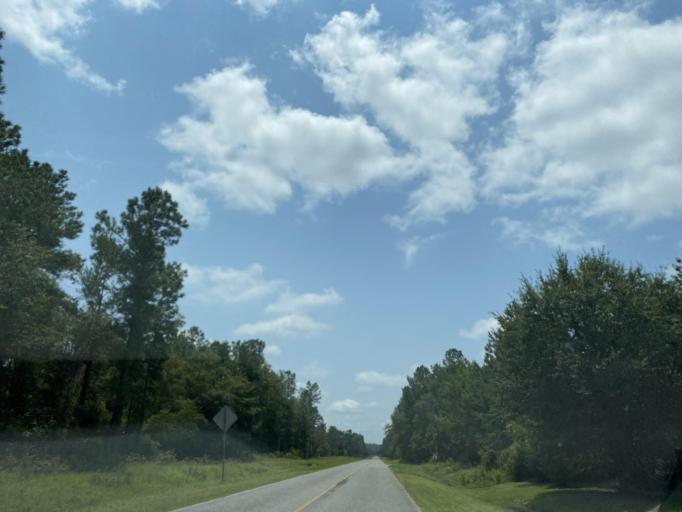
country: US
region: Georgia
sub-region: Telfair County
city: Lumber City
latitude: 31.9791
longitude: -82.7026
